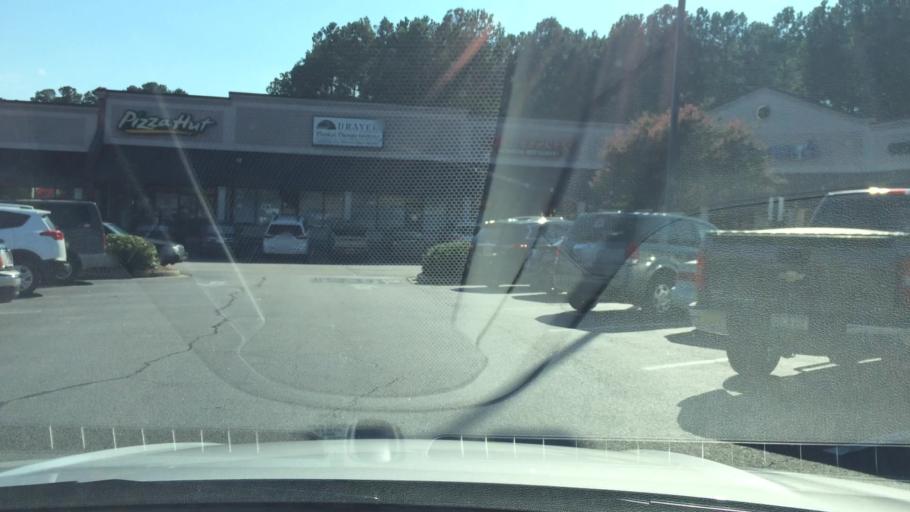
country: US
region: South Carolina
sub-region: Lexington County
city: Irmo
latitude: 34.0868
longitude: -81.1860
